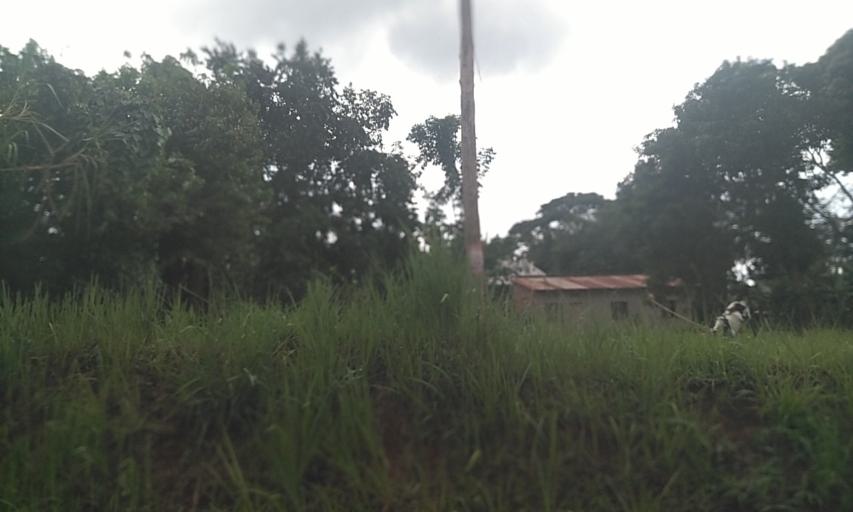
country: UG
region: Central Region
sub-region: Wakiso District
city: Wakiso
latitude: 0.3553
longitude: 32.4610
